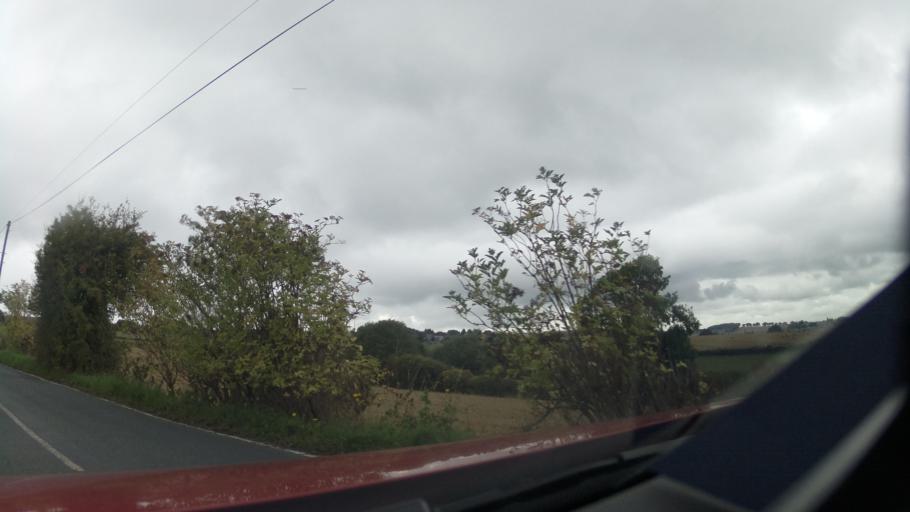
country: GB
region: England
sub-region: Kirklees
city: Clayton West
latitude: 53.6131
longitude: -1.6164
